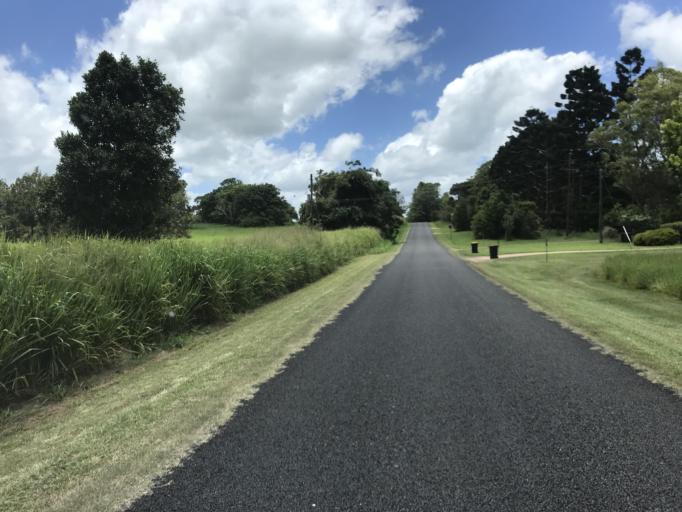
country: AU
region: Queensland
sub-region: Tablelands
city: Atherton
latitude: -17.3375
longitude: 145.5834
